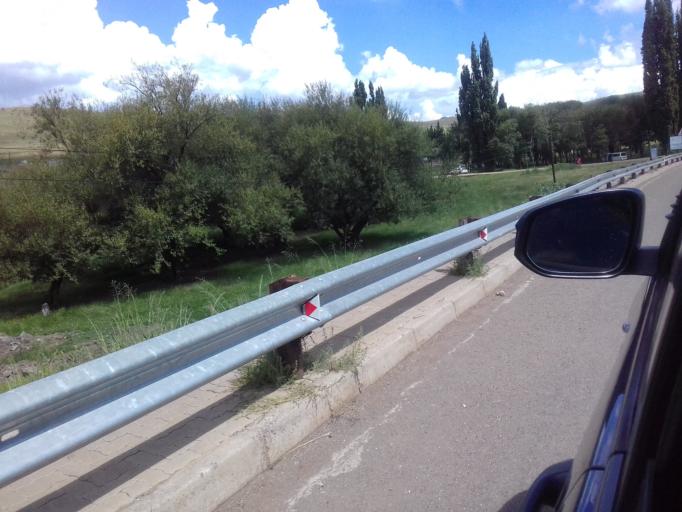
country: LS
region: Thaba-Tseka
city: Thaba-Tseka
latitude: -29.5215
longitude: 28.6034
